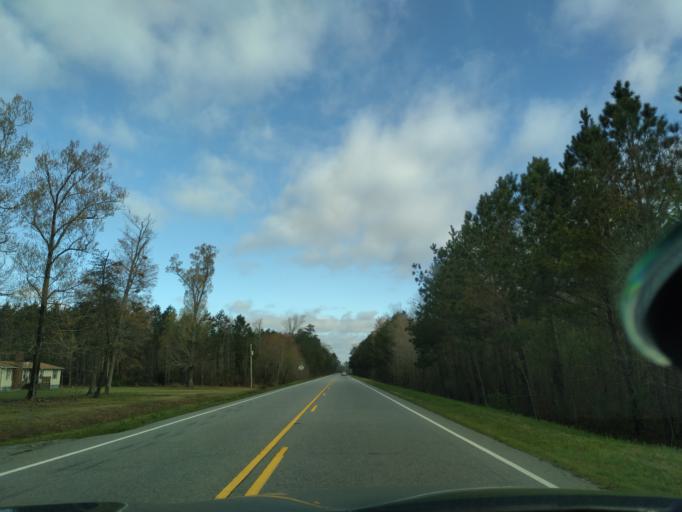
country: US
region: North Carolina
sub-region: Washington County
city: Plymouth
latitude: 35.9856
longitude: -76.7667
